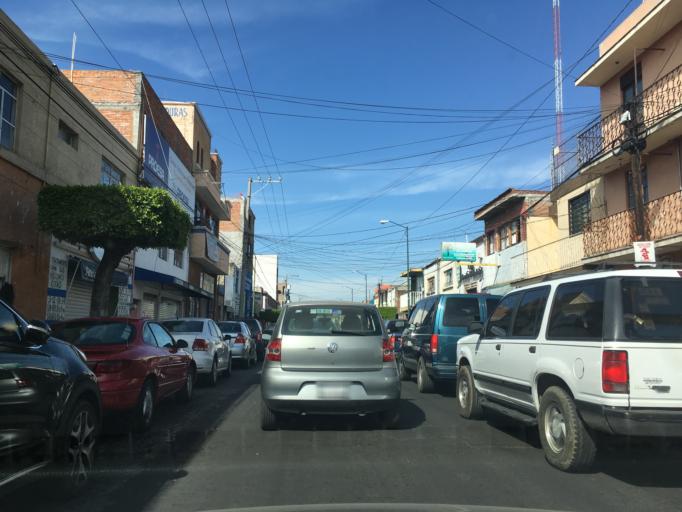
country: MX
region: Michoacan
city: Morelia
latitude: 19.6940
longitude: -101.1906
